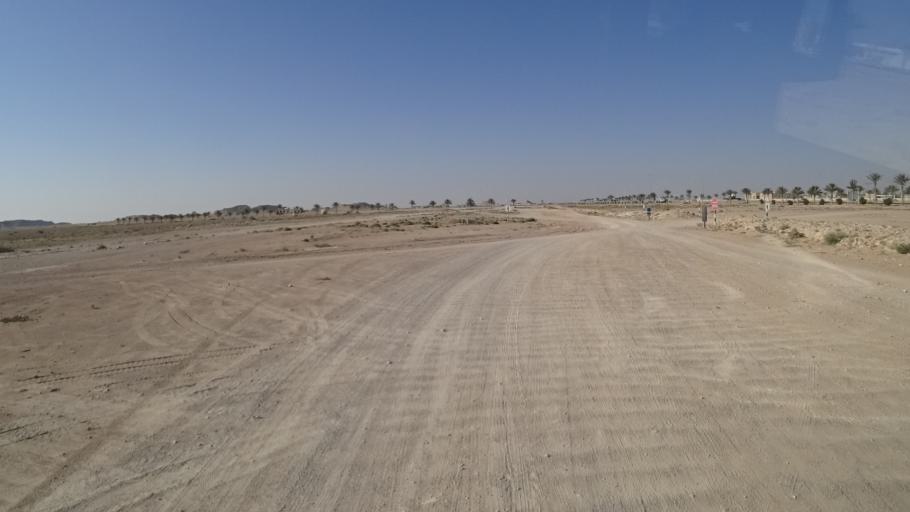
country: OM
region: Zufar
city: Salalah
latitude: 17.6091
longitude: 54.0323
